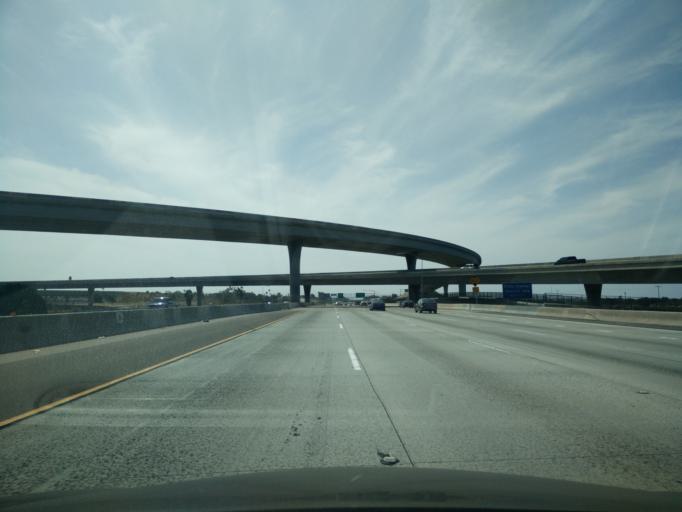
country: US
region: California
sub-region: San Diego County
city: Chula Vista
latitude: 32.6522
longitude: -117.1048
